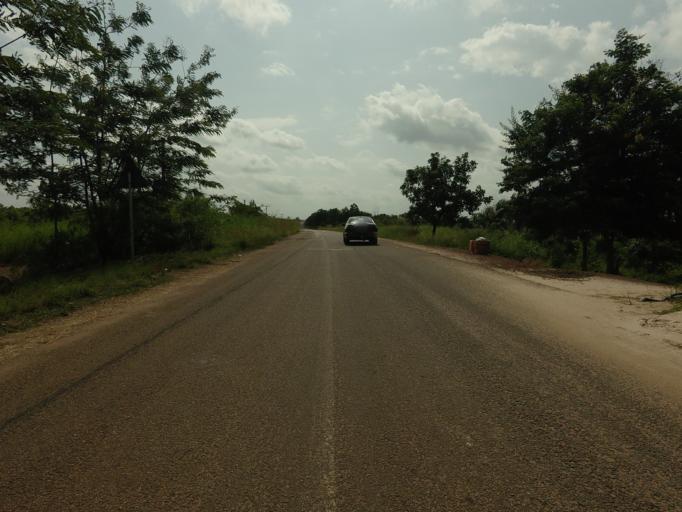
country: TG
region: Maritime
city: Lome
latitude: 6.2691
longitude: 0.9471
